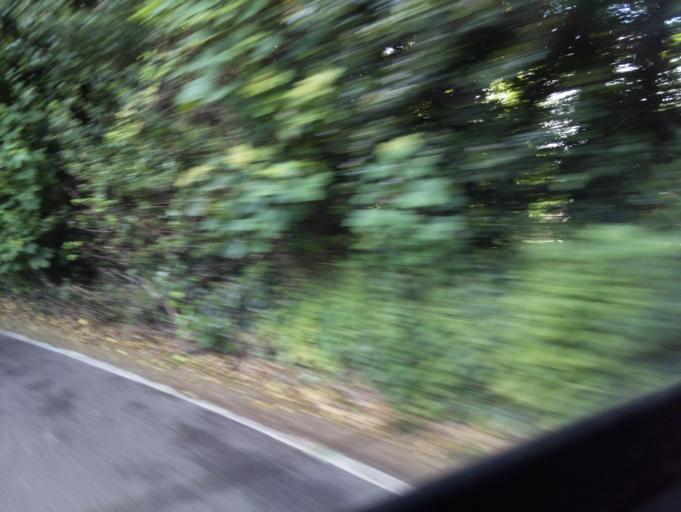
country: GB
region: England
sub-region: Hertfordshire
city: Chorleywood
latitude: 51.6544
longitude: -0.4780
